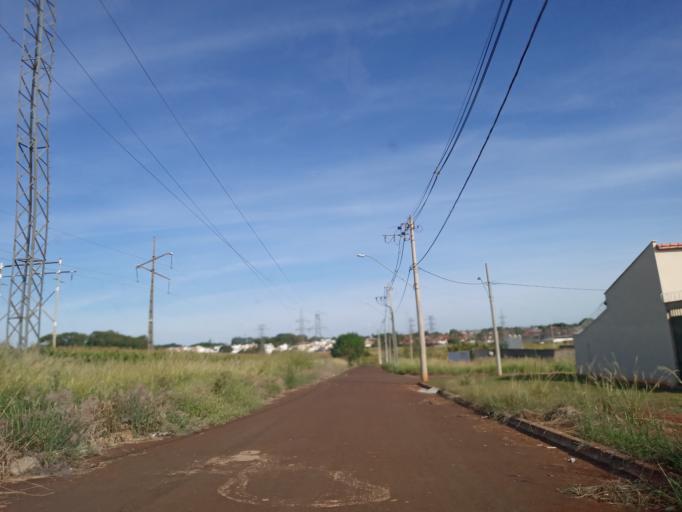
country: BR
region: Minas Gerais
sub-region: Ituiutaba
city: Ituiutaba
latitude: -18.9591
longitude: -49.4478
